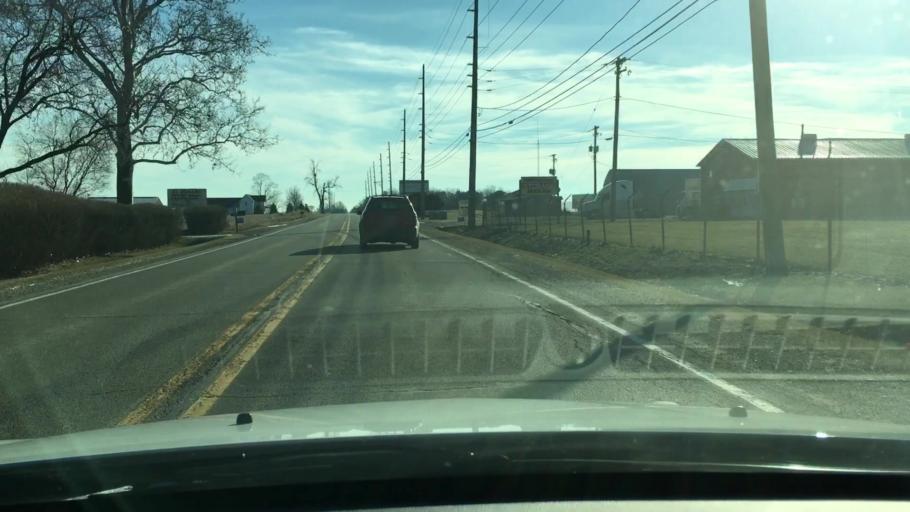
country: US
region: Illinois
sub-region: LaSalle County
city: Mendota
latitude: 41.5375
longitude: -89.1277
